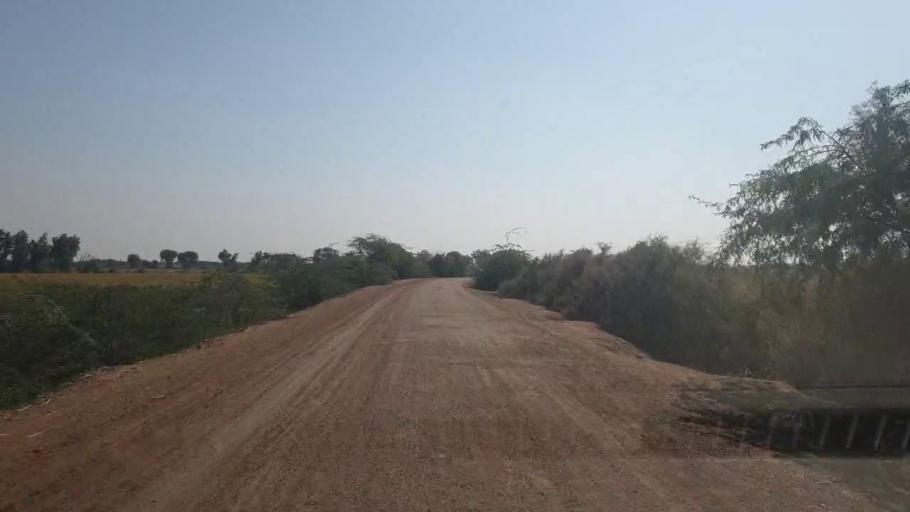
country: PK
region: Sindh
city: Badin
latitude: 24.5691
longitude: 68.8459
